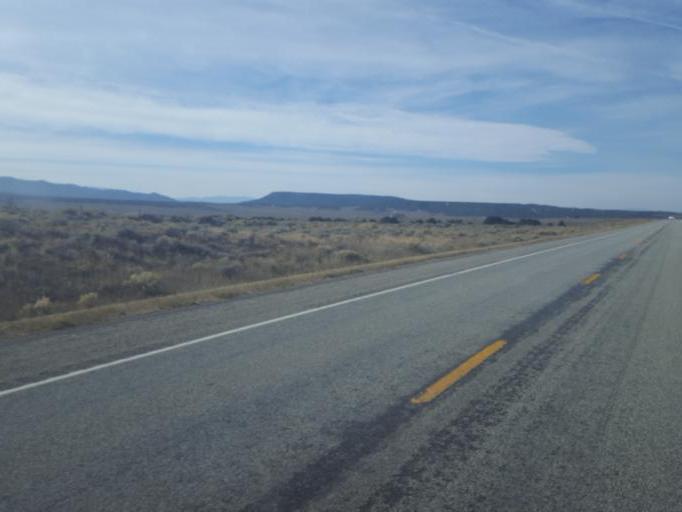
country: US
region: Colorado
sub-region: Costilla County
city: San Luis
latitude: 37.4603
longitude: -105.3591
